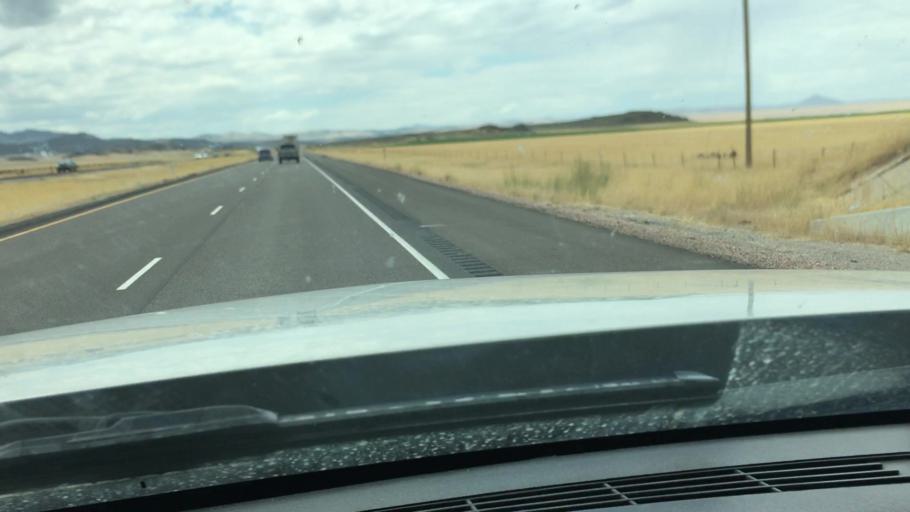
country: US
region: Utah
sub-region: Millard County
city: Fillmore
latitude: 38.8323
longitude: -112.4812
